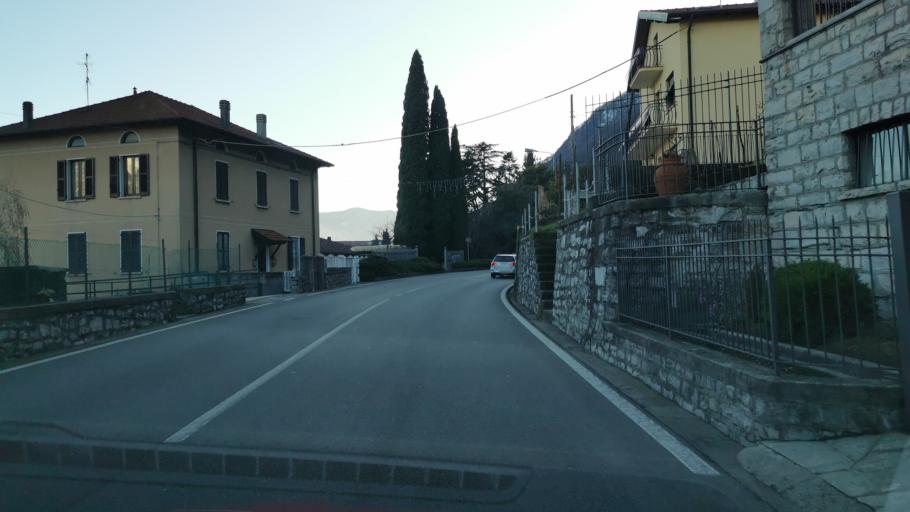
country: IT
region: Lombardy
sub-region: Provincia di Como
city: San Siro
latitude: 46.0583
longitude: 9.2610
